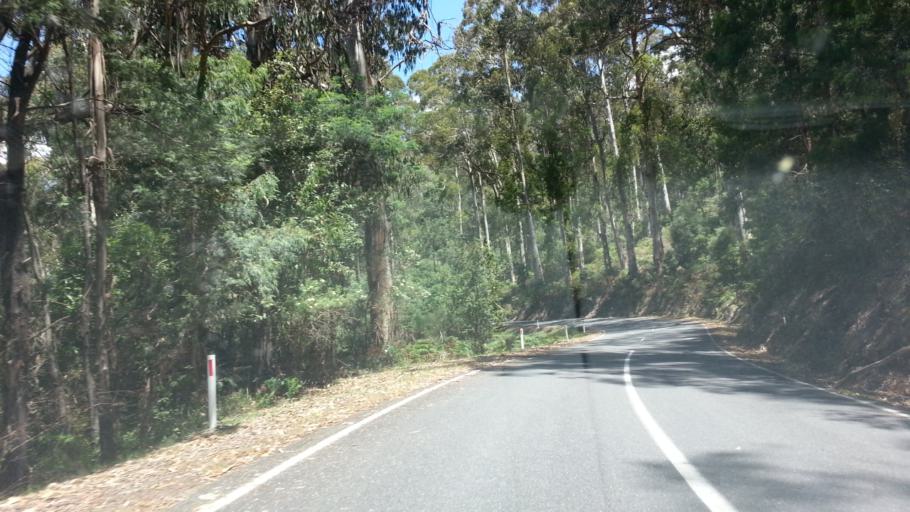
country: AU
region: Victoria
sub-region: Alpine
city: Mount Beauty
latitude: -36.7771
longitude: 147.2157
